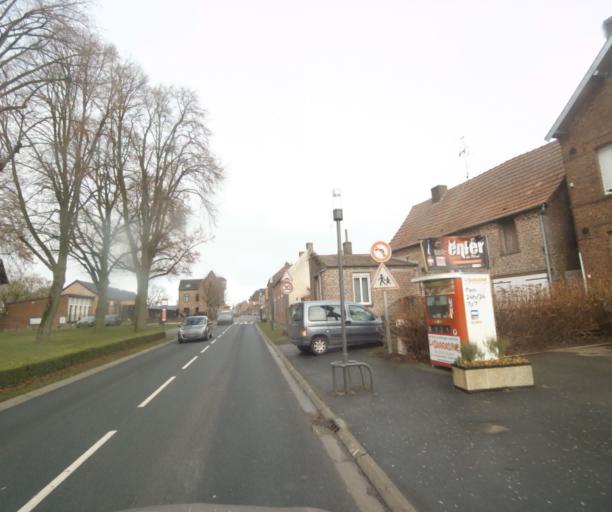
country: FR
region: Nord-Pas-de-Calais
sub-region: Departement du Nord
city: Vendegies-sur-Ecaillon
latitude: 50.2873
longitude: 3.5135
